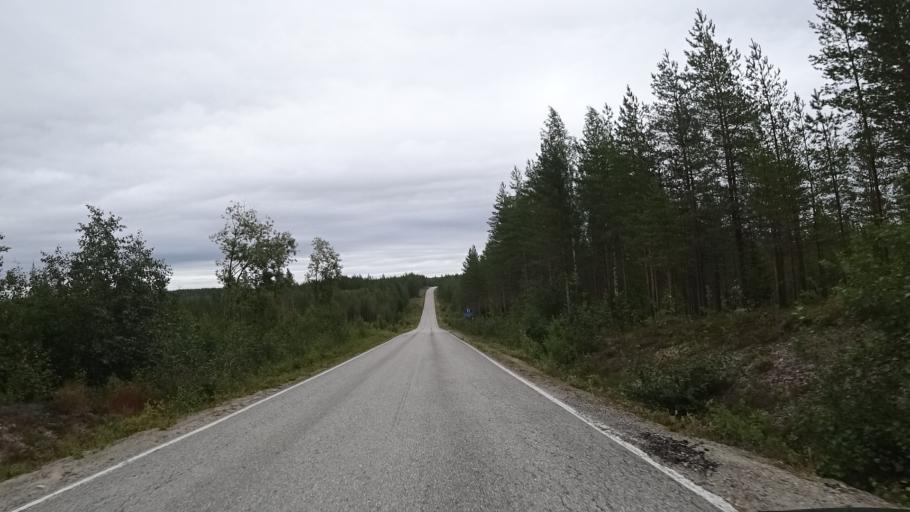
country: FI
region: North Karelia
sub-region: Pielisen Karjala
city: Lieksa
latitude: 63.3791
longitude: 30.3150
